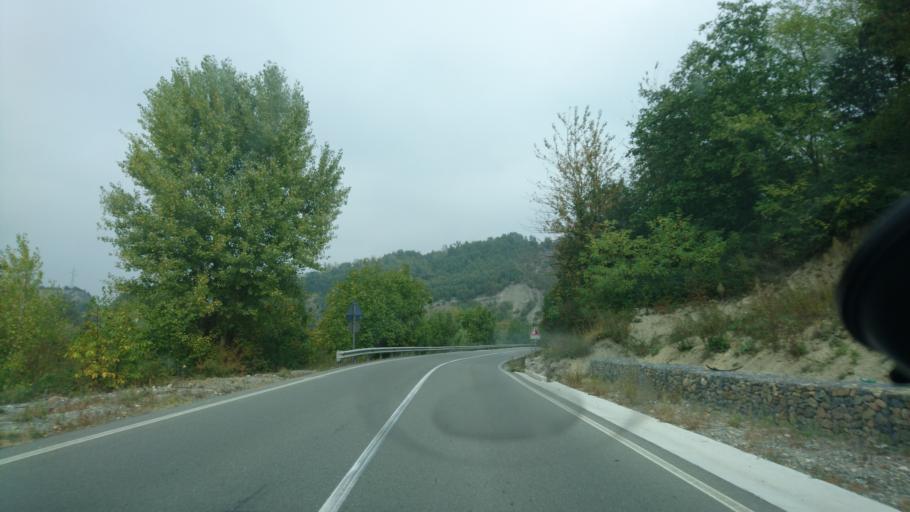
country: IT
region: Piedmont
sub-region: Provincia di Asti
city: Mombaldone
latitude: 44.5705
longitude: 8.3489
